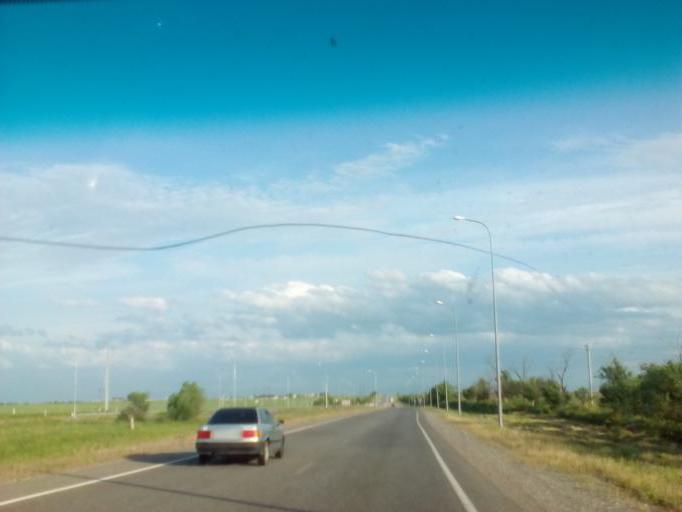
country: KZ
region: Ongtustik Qazaqstan
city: Temirlanovka
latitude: 42.5270
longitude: 69.3424
